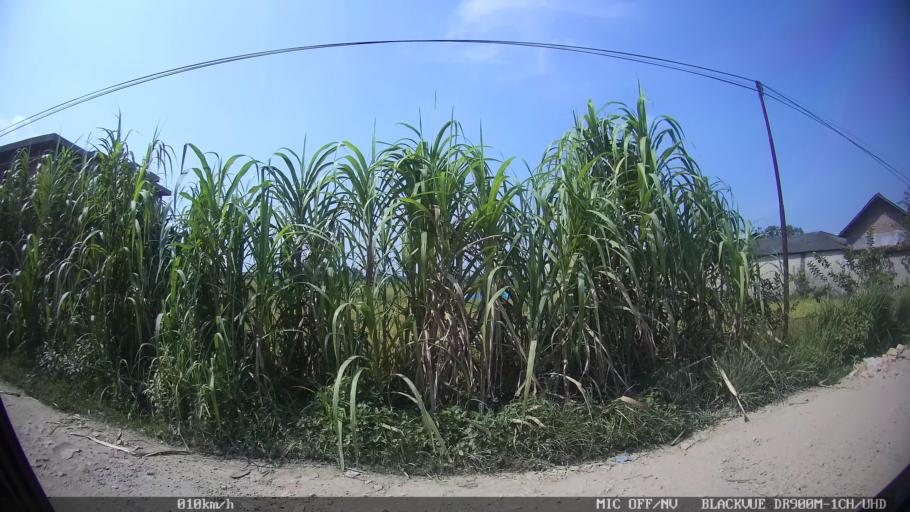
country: ID
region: Lampung
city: Natar
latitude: -5.2665
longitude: 105.1943
